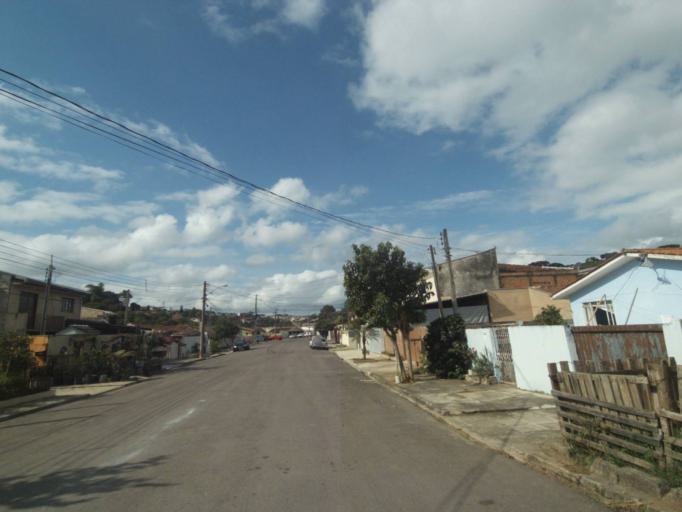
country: BR
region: Parana
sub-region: Curitiba
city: Curitiba
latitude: -25.3828
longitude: -49.3014
